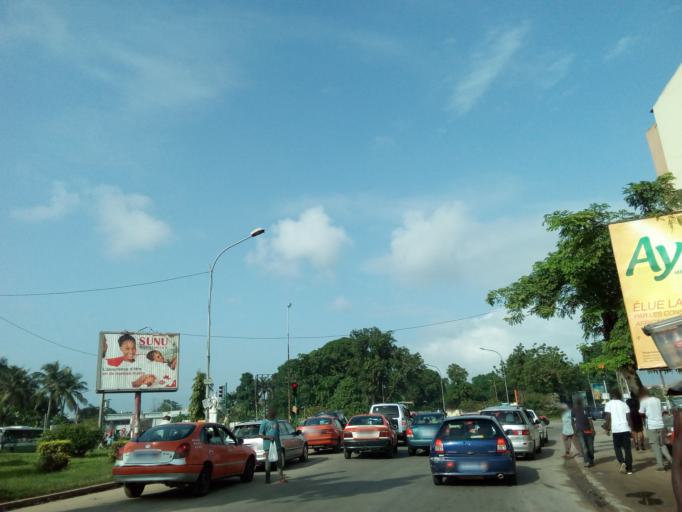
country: CI
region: Lagunes
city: Abidjan
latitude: 5.2957
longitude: -4.0036
